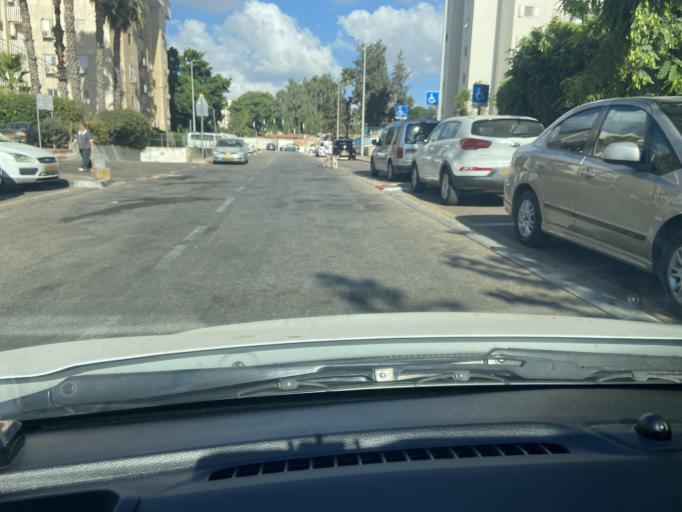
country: IL
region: Central District
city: Yehud
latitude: 32.0310
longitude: 34.8923
